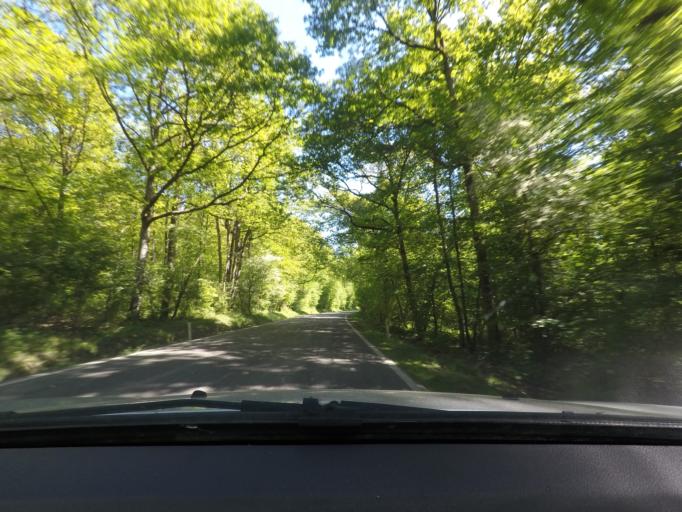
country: BE
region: Wallonia
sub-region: Province de Namur
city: Rochefort
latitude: 50.1879
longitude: 5.1226
